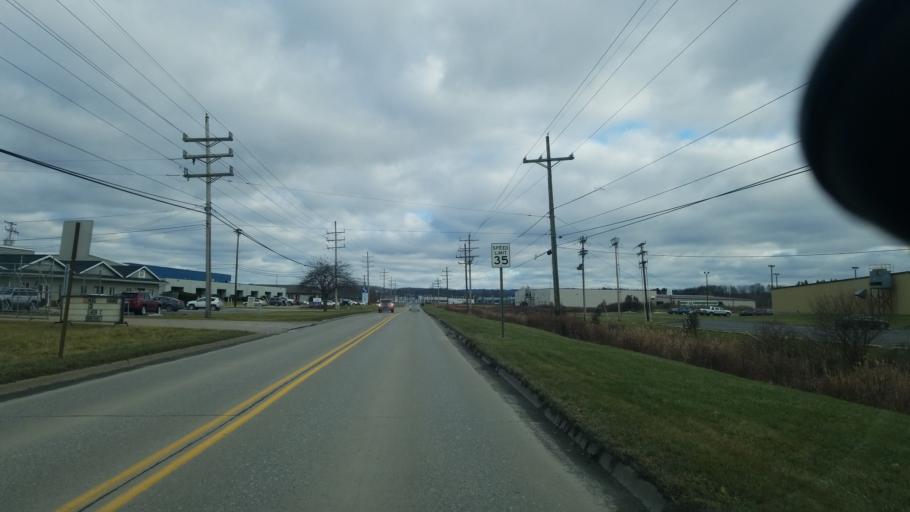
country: US
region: Pennsylvania
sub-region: Clearfield County
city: DuBois
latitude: 41.1225
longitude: -78.7474
